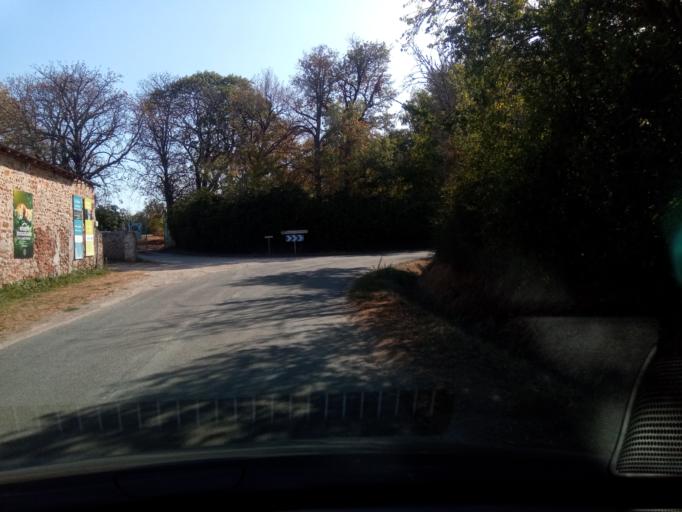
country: FR
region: Centre
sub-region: Departement de l'Indre
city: Mezieres-en-Brenne
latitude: 46.7201
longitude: 1.1737
